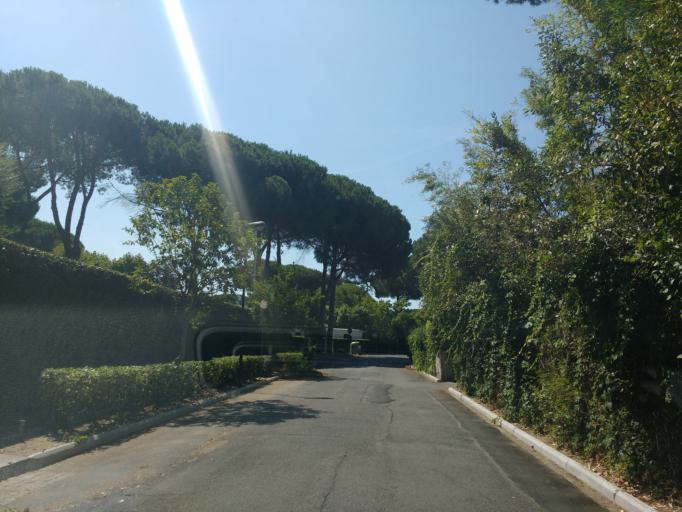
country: IT
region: Latium
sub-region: Citta metropolitana di Roma Capitale
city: Acilia-Castel Fusano-Ostia Antica
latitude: 41.7506
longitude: 12.3585
